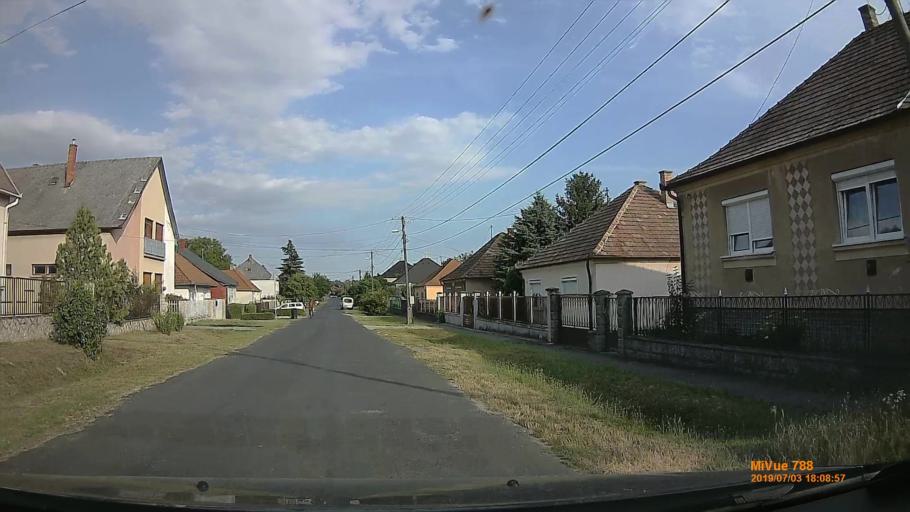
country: HU
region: Gyor-Moson-Sopron
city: Gyor
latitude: 47.6376
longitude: 17.5948
